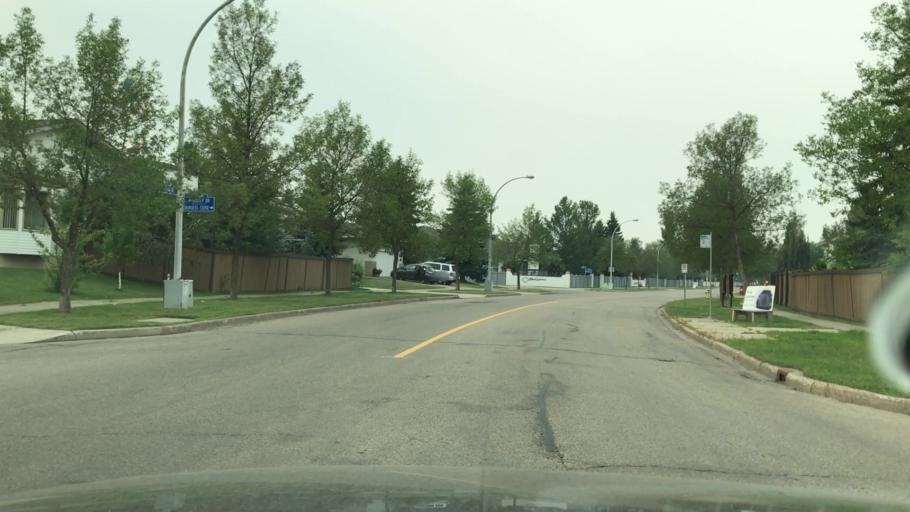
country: CA
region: Alberta
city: Edmonton
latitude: 53.4692
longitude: -113.5721
